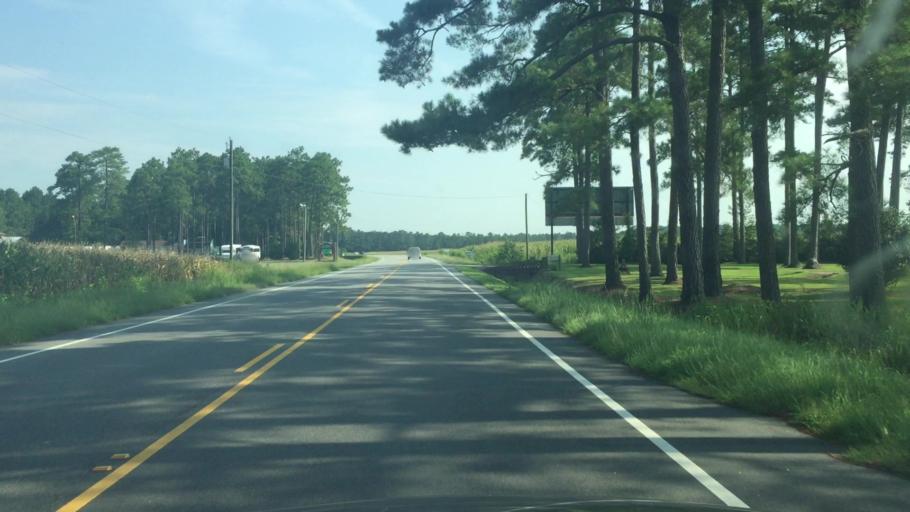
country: US
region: North Carolina
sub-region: Columbus County
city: Tabor City
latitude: 34.1745
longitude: -78.8409
